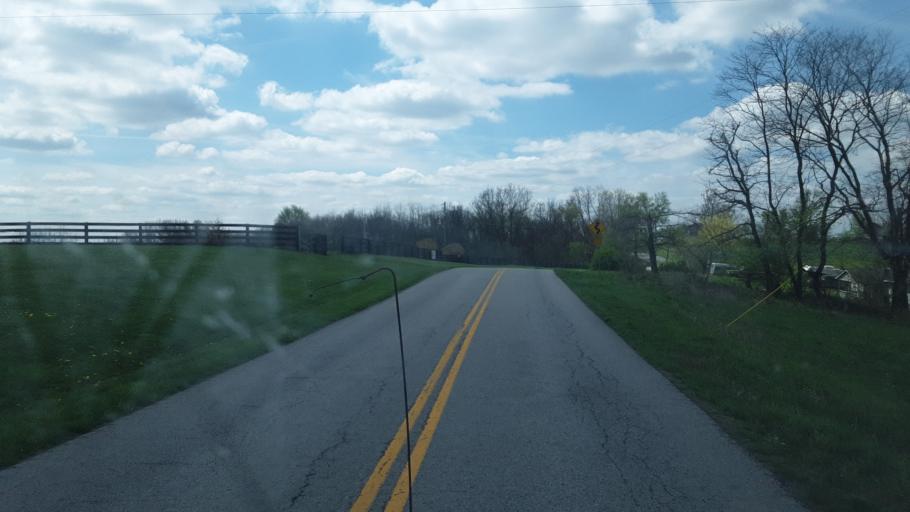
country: US
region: Kentucky
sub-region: Owen County
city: Owenton
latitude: 38.6323
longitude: -84.7785
